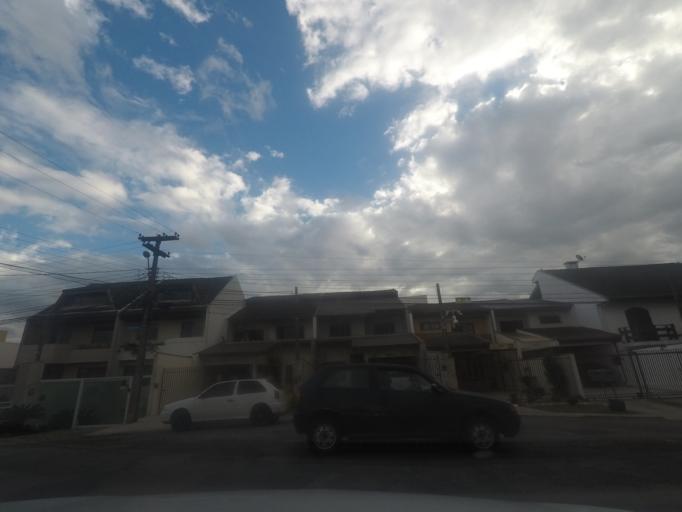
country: BR
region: Parana
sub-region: Pinhais
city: Pinhais
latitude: -25.4656
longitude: -49.2210
